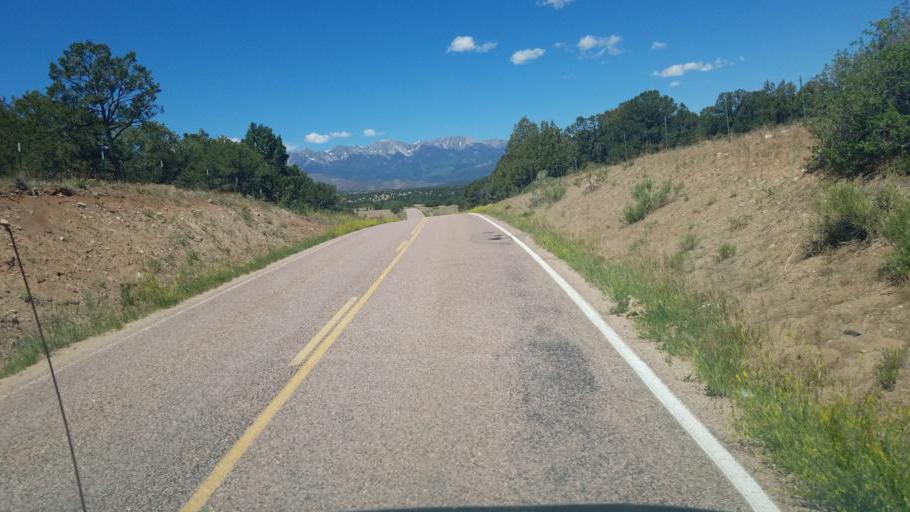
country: US
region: Colorado
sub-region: Custer County
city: Westcliffe
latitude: 38.3111
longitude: -105.6483
